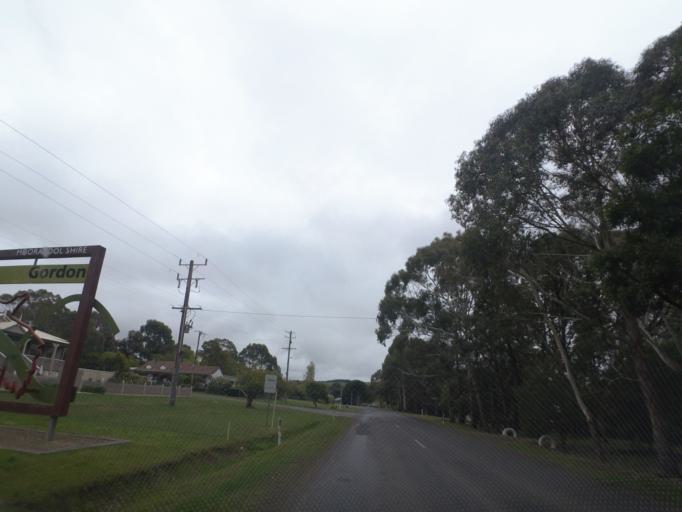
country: AU
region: Victoria
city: Brown Hill
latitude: -37.5842
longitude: 144.1123
